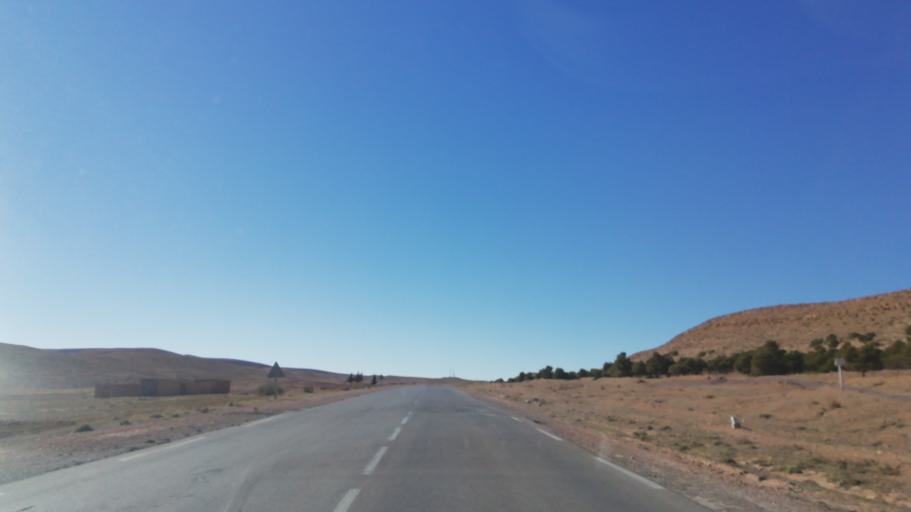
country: DZ
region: El Bayadh
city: El Bayadh
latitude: 33.6791
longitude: 1.4513
